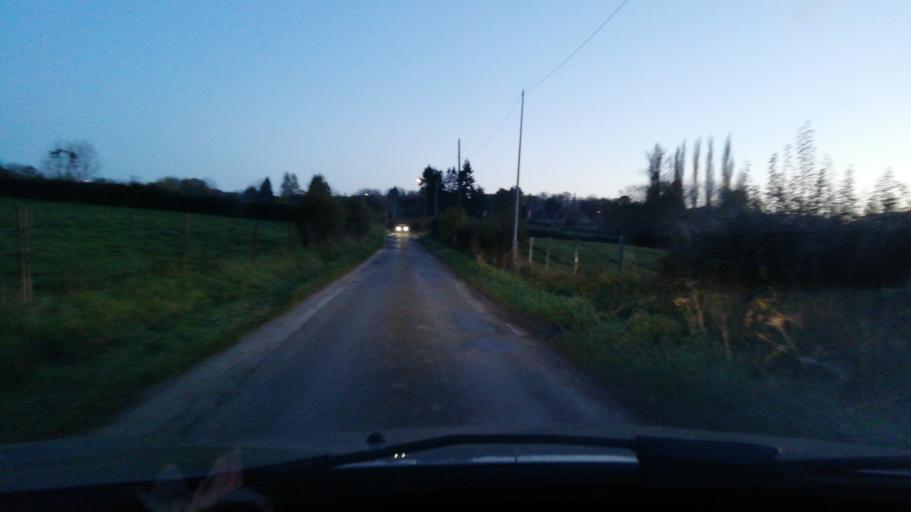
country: FR
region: Nord-Pas-de-Calais
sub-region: Departement du Nord
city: Marpent
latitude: 50.2549
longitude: 4.0912
